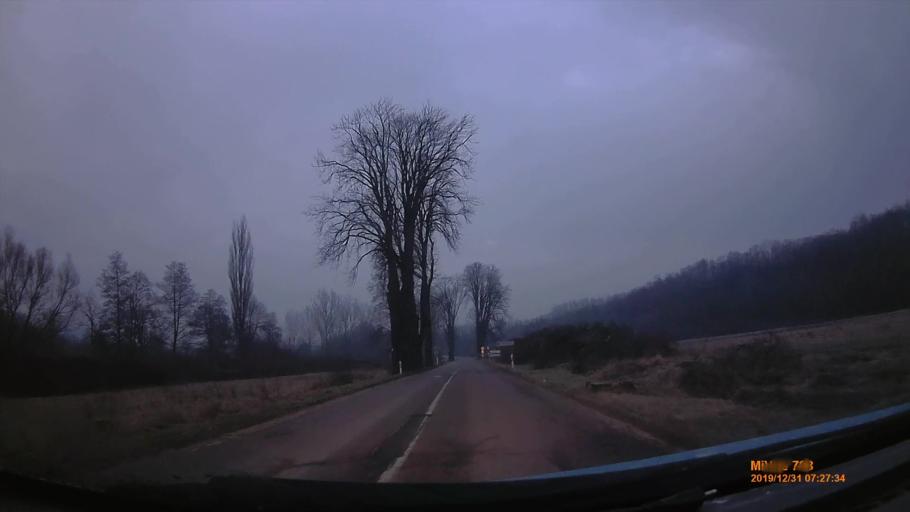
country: HU
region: Heves
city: Matraderecske
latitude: 47.9260
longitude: 20.0855
